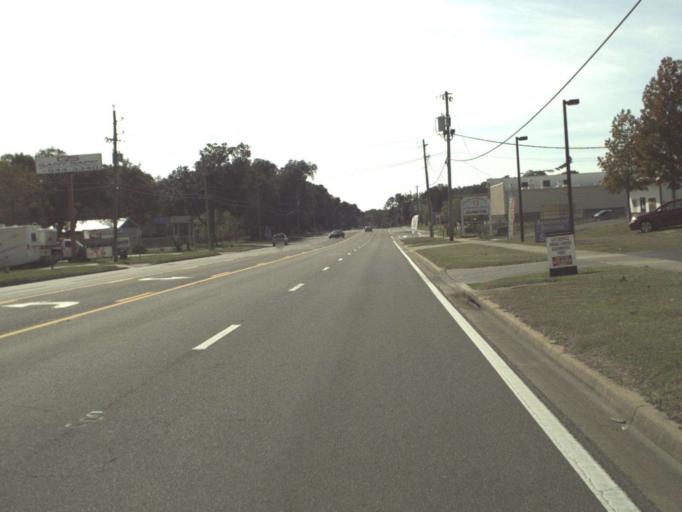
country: US
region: Florida
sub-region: Escambia County
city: Bellview
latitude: 30.4794
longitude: -87.3068
